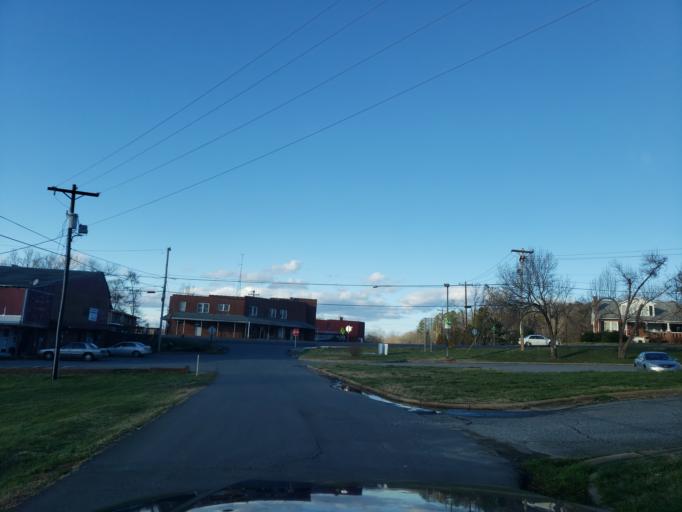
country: US
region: North Carolina
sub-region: Cleveland County
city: Shelby
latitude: 35.4172
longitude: -81.5587
